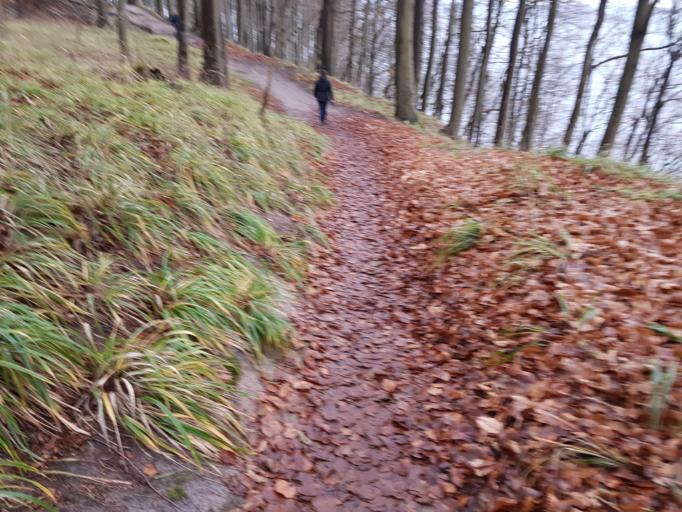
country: DE
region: Mecklenburg-Vorpommern
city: Ostseebad Sellin
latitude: 54.4011
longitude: 13.6682
